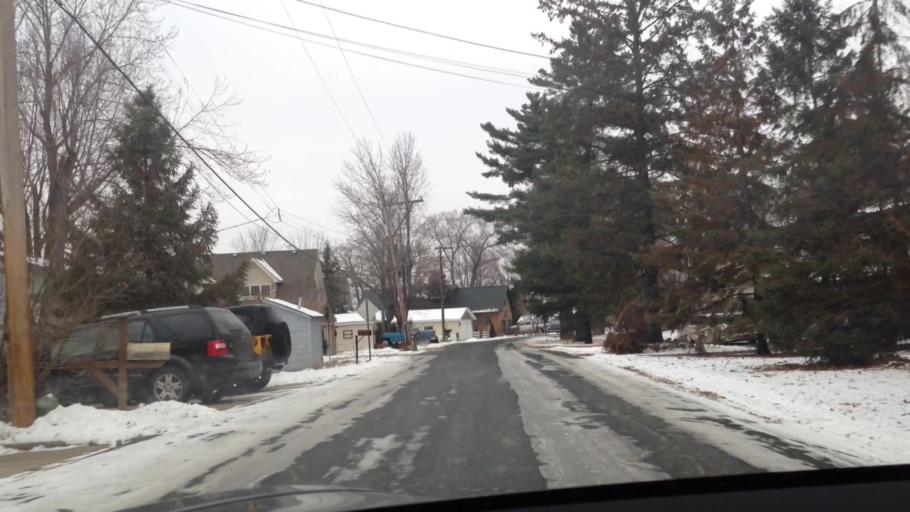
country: US
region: Minnesota
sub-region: Washington County
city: Forest Lake
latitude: 45.2660
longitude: -92.9420
